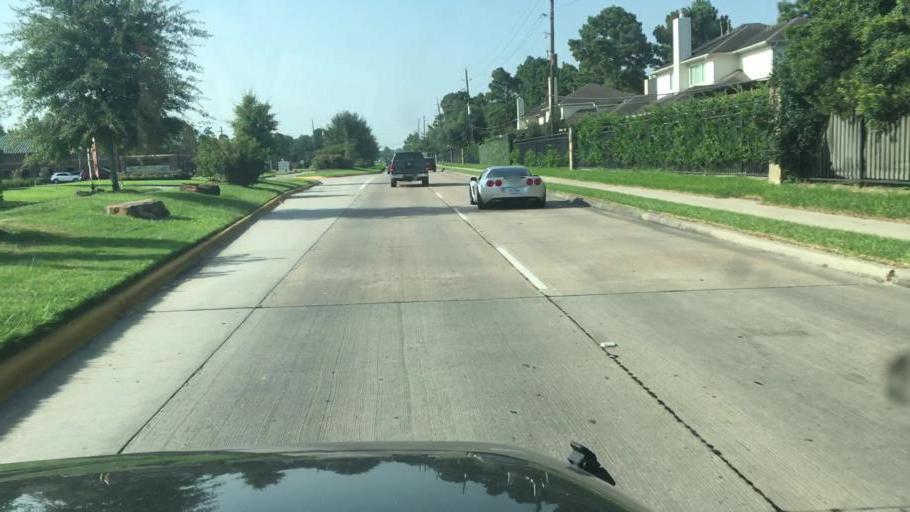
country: US
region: Texas
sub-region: Harris County
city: Atascocita
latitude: 29.9858
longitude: -95.1614
